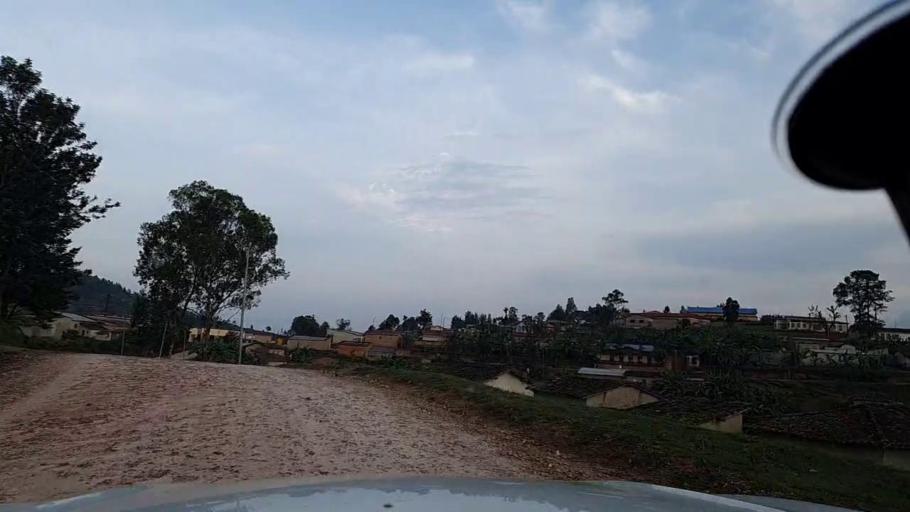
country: RW
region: Southern Province
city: Nyanza
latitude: -2.2216
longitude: 29.6462
